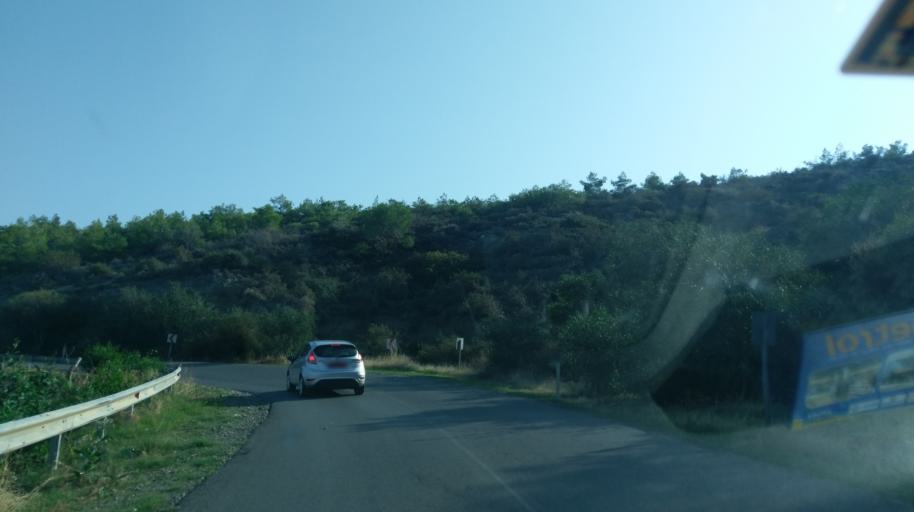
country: CY
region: Lefkosia
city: Lefka
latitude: 35.1522
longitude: 32.7929
